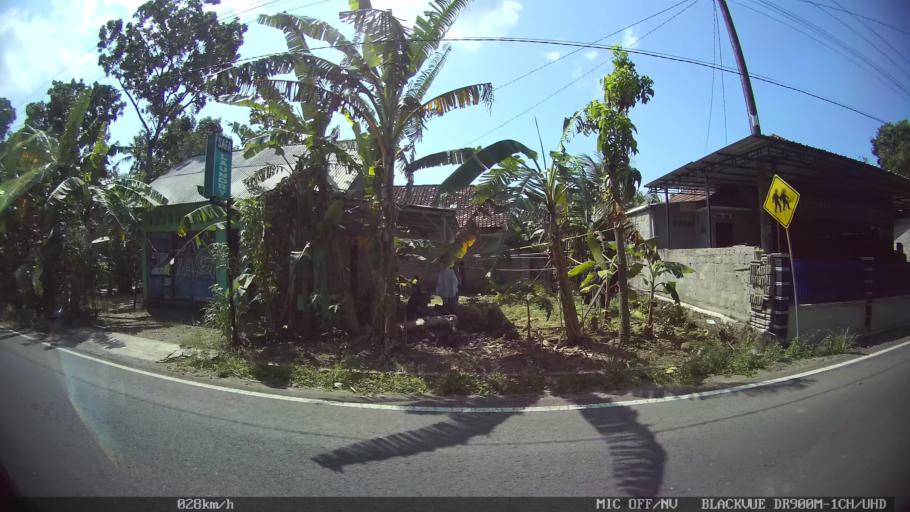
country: ID
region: Daerah Istimewa Yogyakarta
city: Pundong
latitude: -7.9870
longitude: 110.3309
